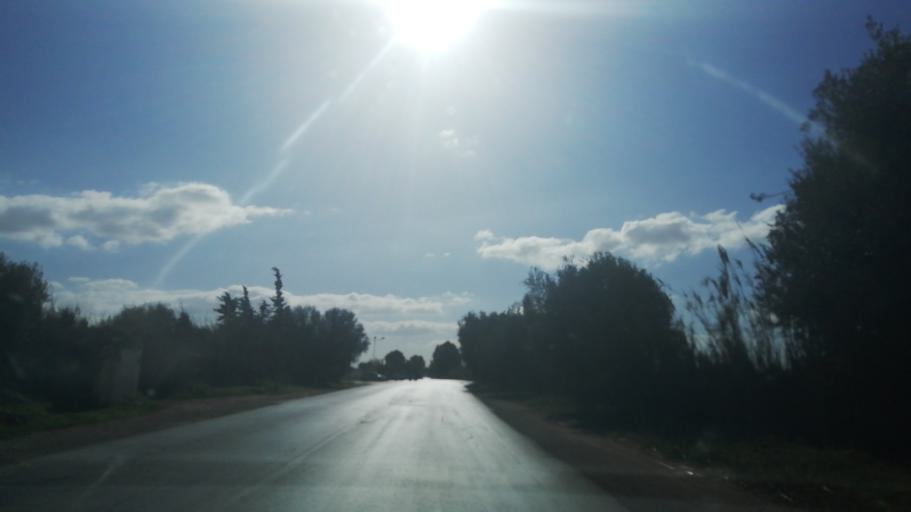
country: DZ
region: Mostaganem
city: Mostaganem
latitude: 35.9650
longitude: 0.2582
